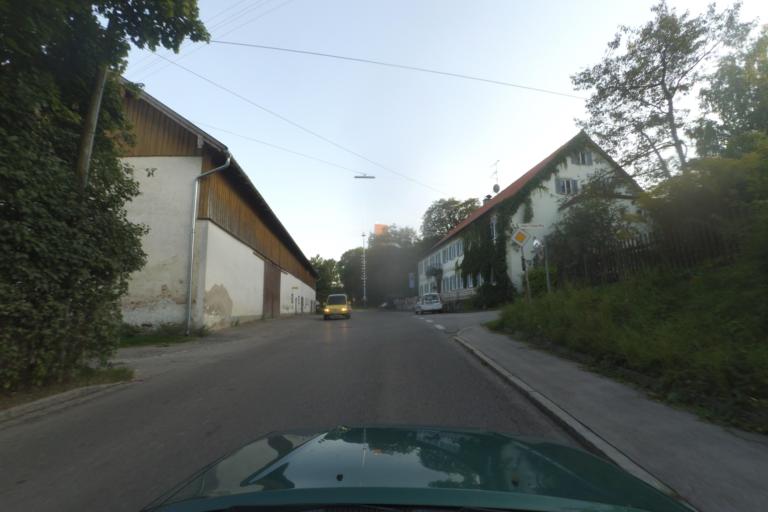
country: DE
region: Bavaria
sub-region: Upper Bavaria
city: Weil
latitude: 48.0984
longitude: 10.9066
